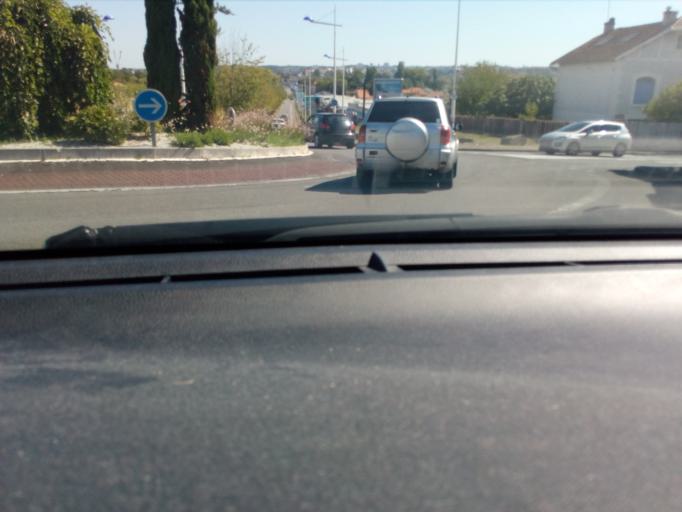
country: FR
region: Poitou-Charentes
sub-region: Departement de la Charente
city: Angouleme
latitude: 45.6641
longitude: 0.1516
